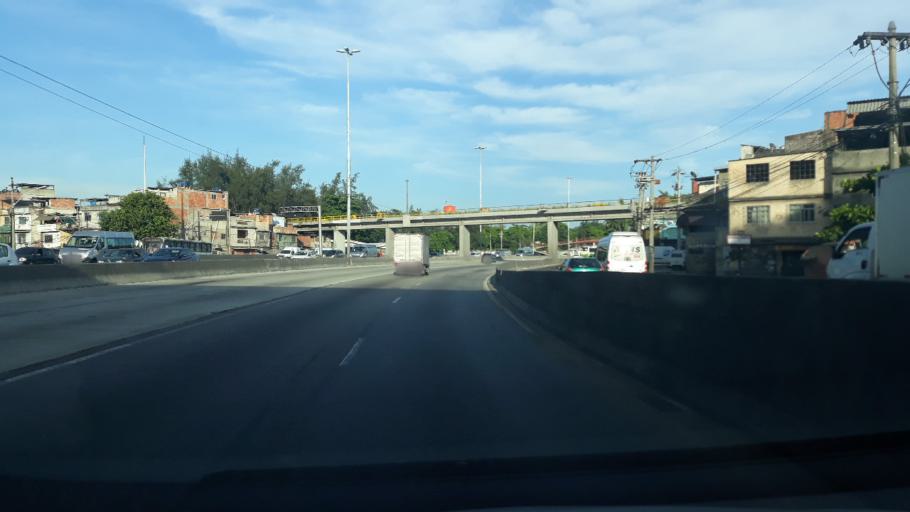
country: BR
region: Rio de Janeiro
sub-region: Rio De Janeiro
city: Rio de Janeiro
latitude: -22.8870
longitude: -43.2327
